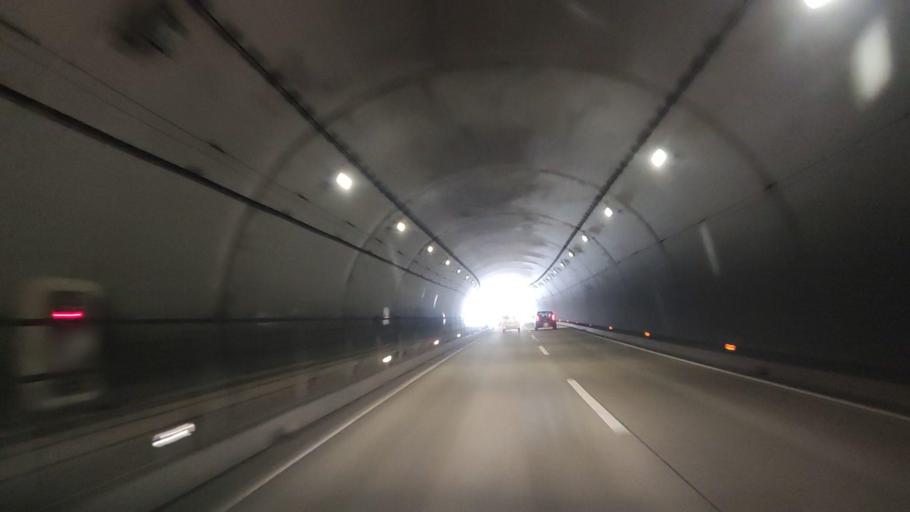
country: JP
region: Gifu
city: Gifu-shi
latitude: 35.4331
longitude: 136.7968
